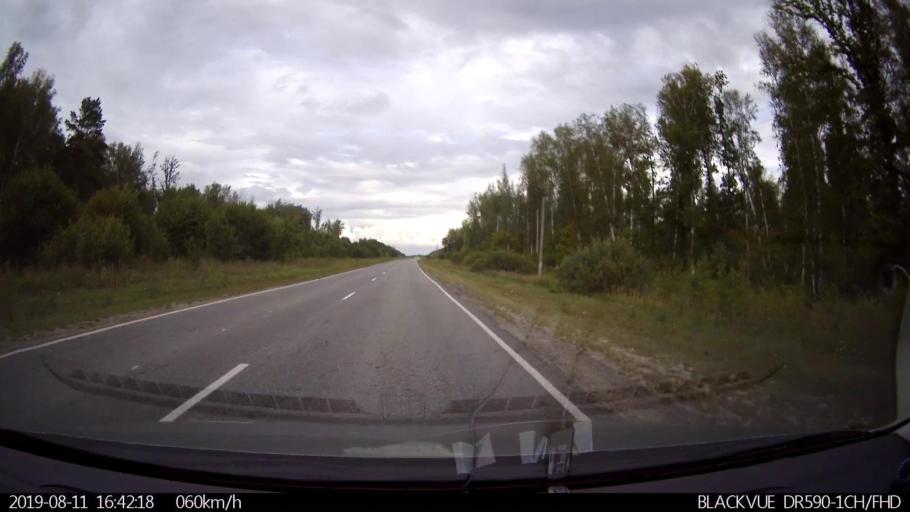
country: RU
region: Ulyanovsk
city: Mayna
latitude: 54.1594
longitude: 47.6611
